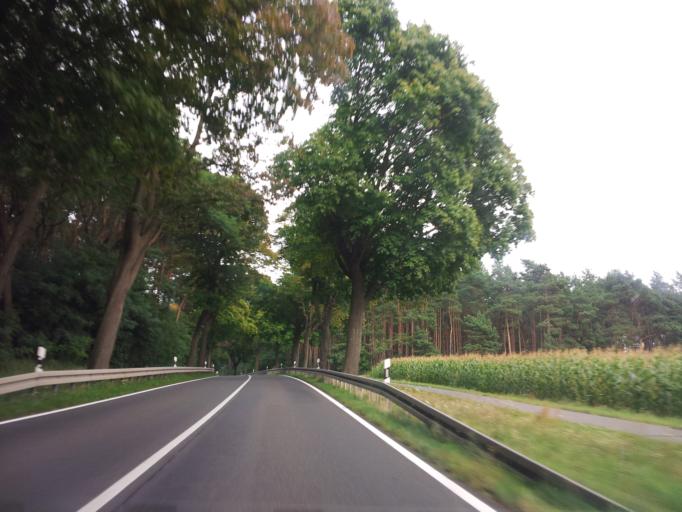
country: DE
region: Brandenburg
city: Niemegk
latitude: 52.0857
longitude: 12.7371
